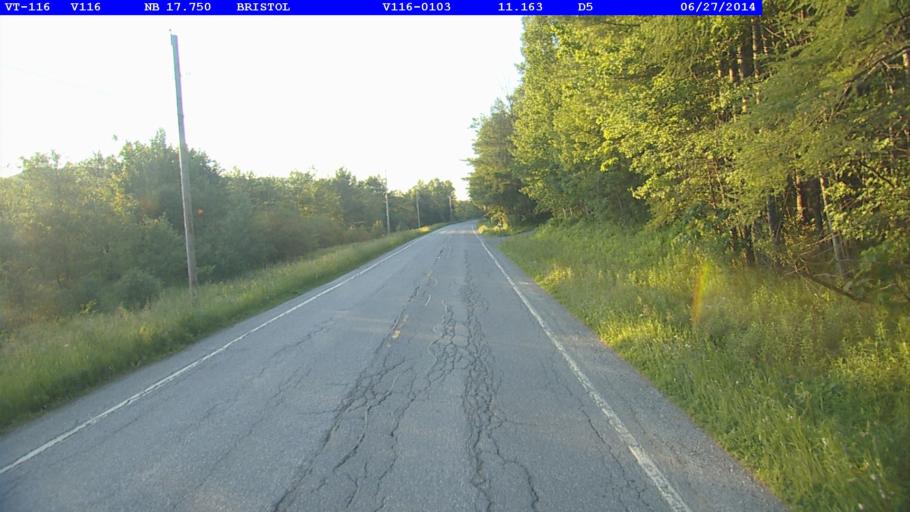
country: US
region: Vermont
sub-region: Addison County
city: Bristol
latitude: 44.1698
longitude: -73.0560
